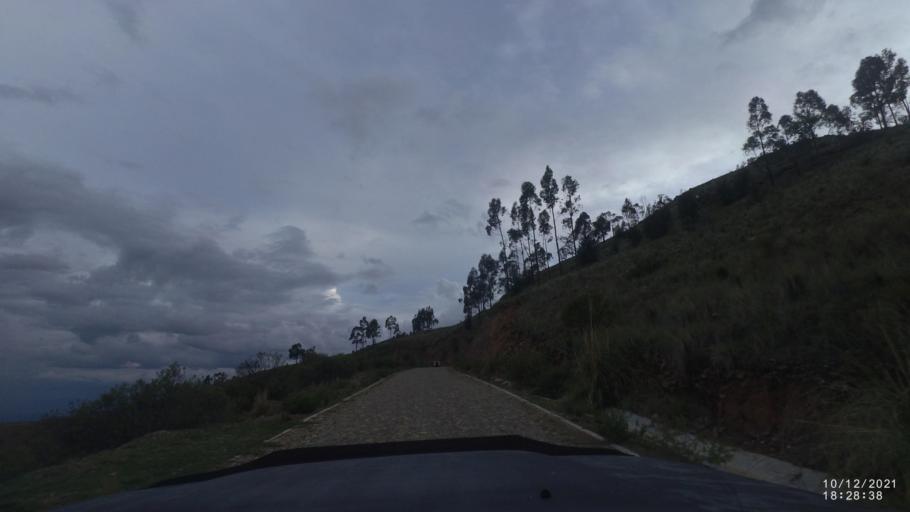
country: BO
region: Cochabamba
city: Tarata
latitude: -17.8093
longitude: -65.9756
